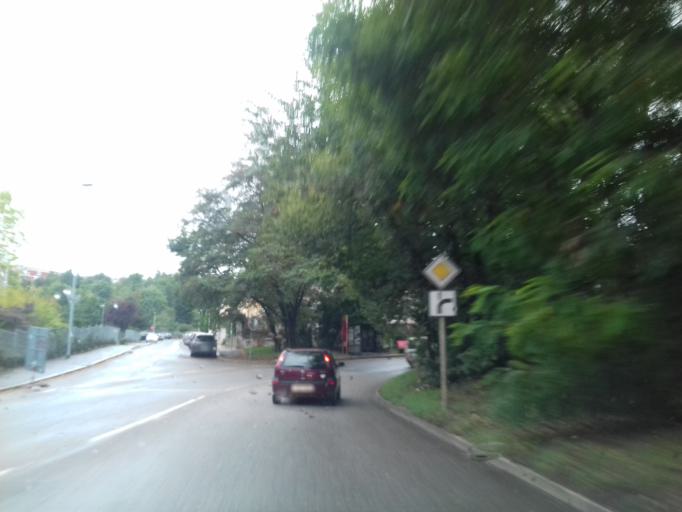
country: CZ
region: Praha
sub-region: Praha 1
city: Mala Strana
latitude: 50.0567
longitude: 14.3702
